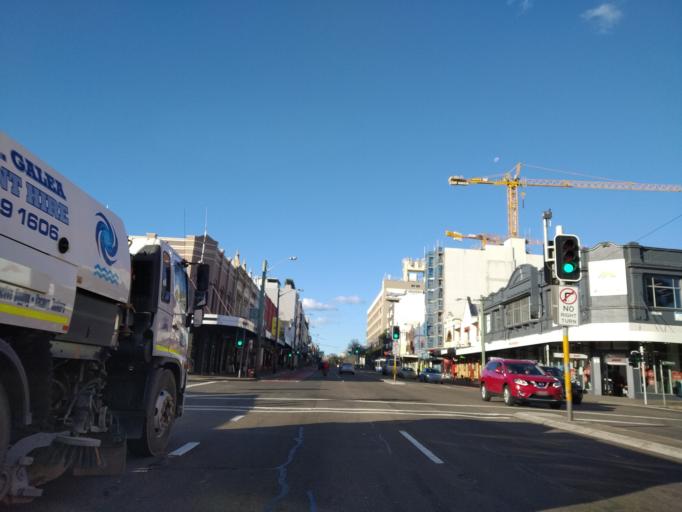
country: AU
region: New South Wales
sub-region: Marrickville
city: Camperdown
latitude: -33.8868
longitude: 151.1763
